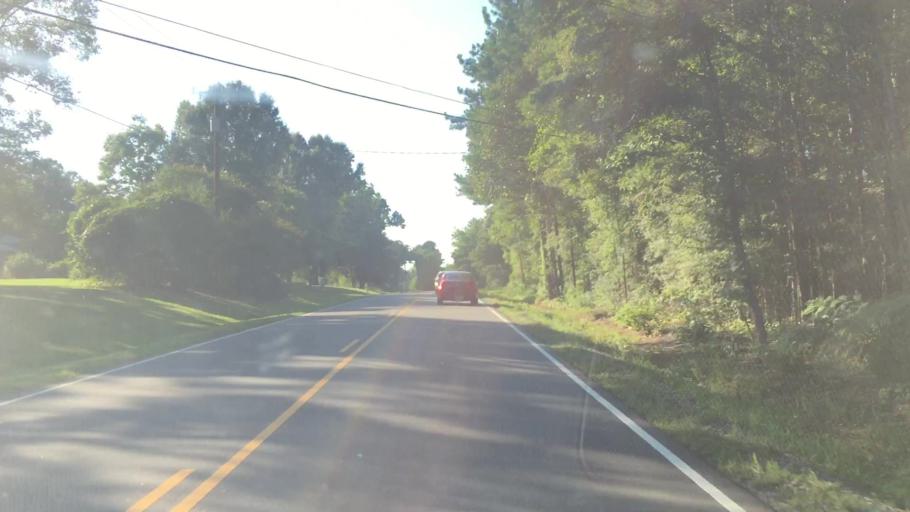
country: US
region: North Carolina
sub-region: Rowan County
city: Enochville
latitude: 35.4704
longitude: -80.7440
